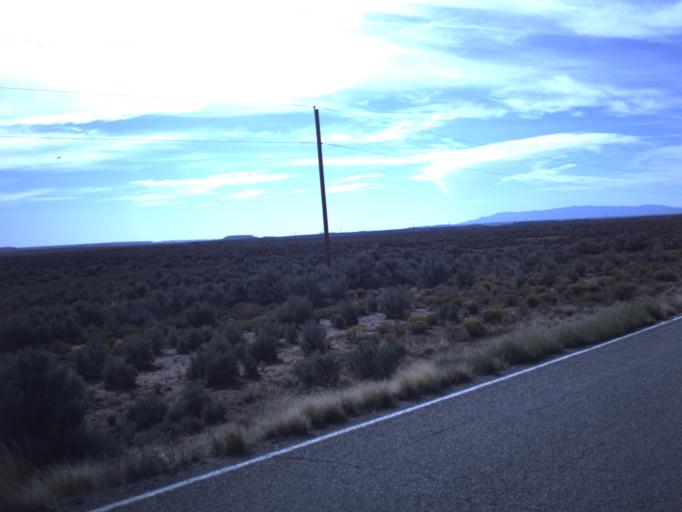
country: US
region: Utah
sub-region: San Juan County
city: Blanding
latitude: 37.4012
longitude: -109.3374
